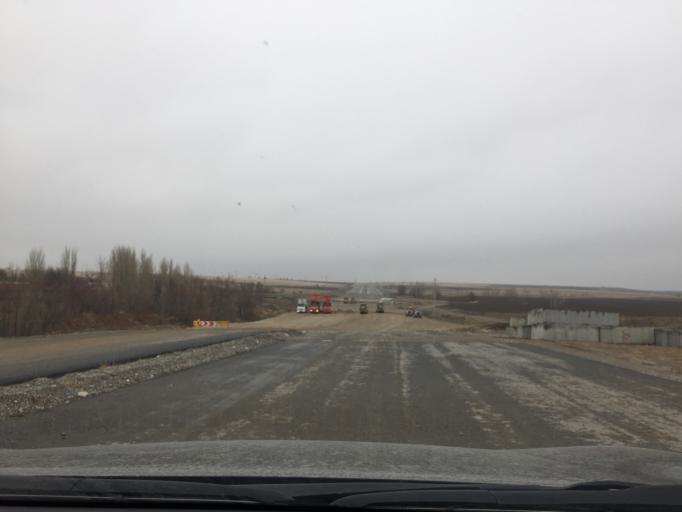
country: KZ
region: Ongtustik Qazaqstan
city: Turar Ryskulov
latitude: 42.5147
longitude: 70.3418
